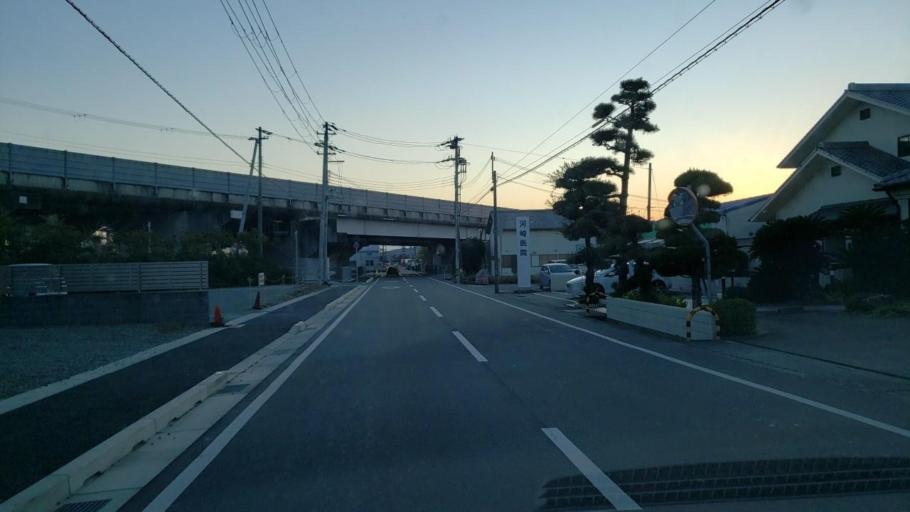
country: JP
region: Hyogo
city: Fukura
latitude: 34.3206
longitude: 134.7719
